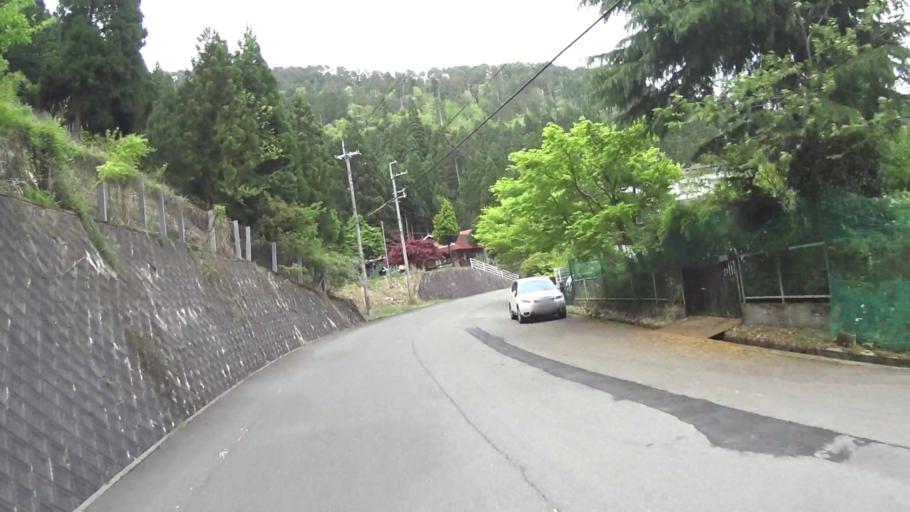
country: JP
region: Kyoto
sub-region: Kyoto-shi
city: Kamigyo-ku
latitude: 35.2188
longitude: 135.7021
